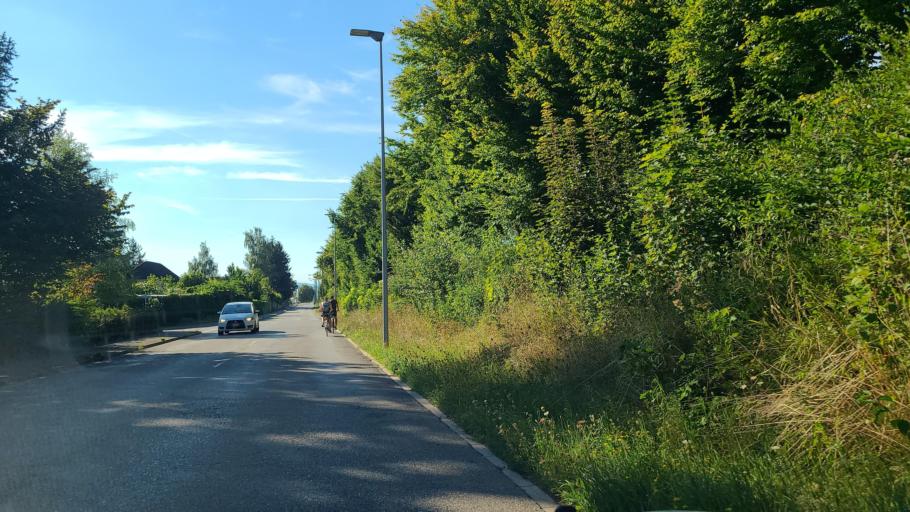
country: CH
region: Zurich
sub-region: Bezirk Affoltern
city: Obfelden / Toussen
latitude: 47.2656
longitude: 8.4283
